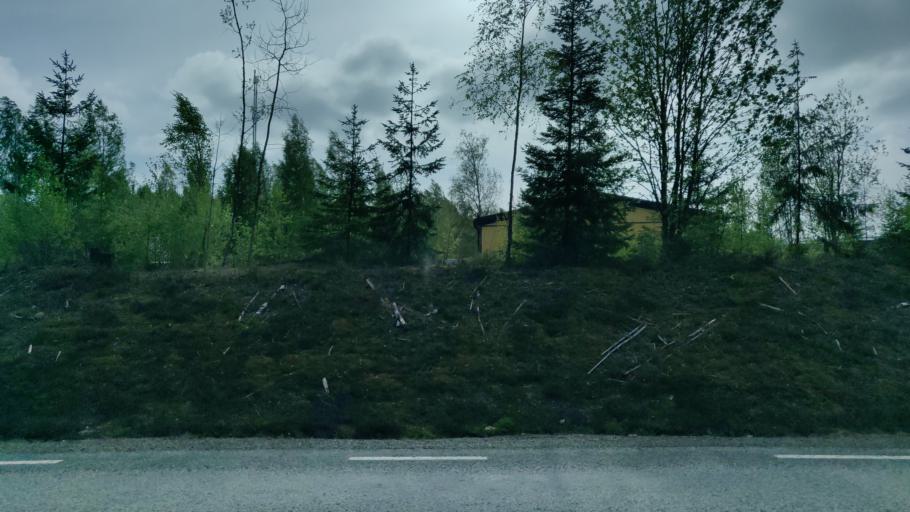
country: SE
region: Vaermland
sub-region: Forshaga Kommun
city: Deje
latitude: 59.6189
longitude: 13.4481
